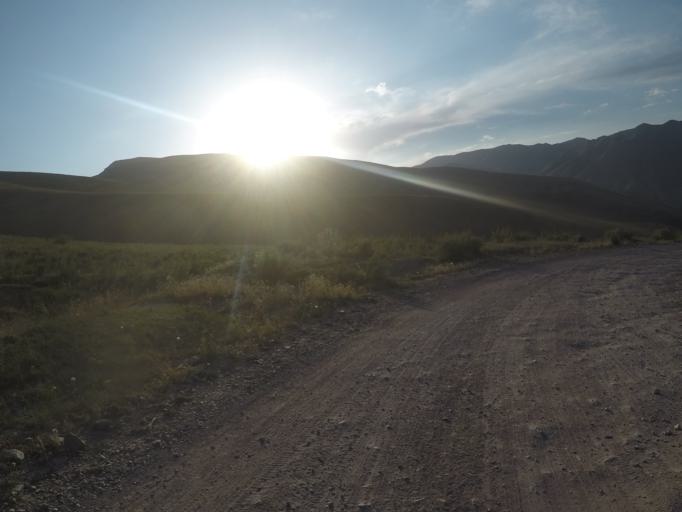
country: KG
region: Chuy
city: Bishkek
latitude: 42.6544
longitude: 74.6541
